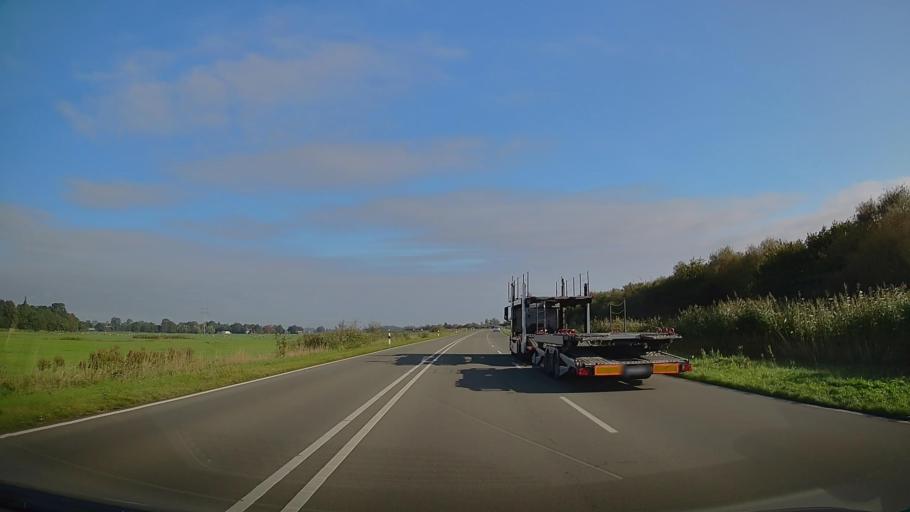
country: DE
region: Lower Saxony
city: Ovelgonne
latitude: 53.3542
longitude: 8.4453
